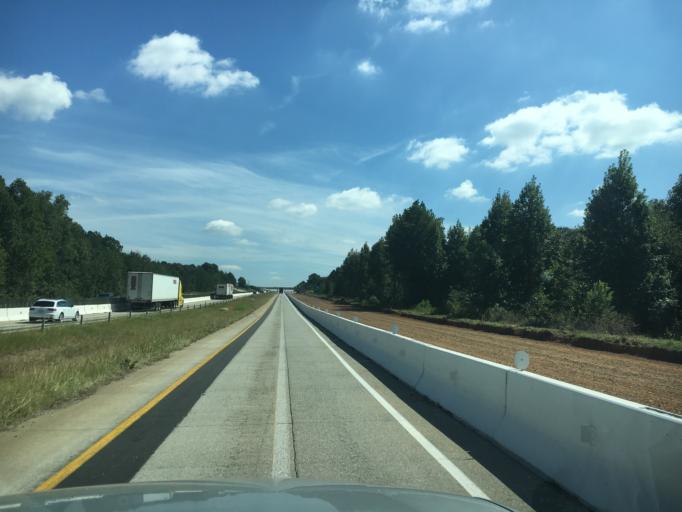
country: US
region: South Carolina
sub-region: Spartanburg County
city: Valley Falls
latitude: 35.0127
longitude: -81.9690
